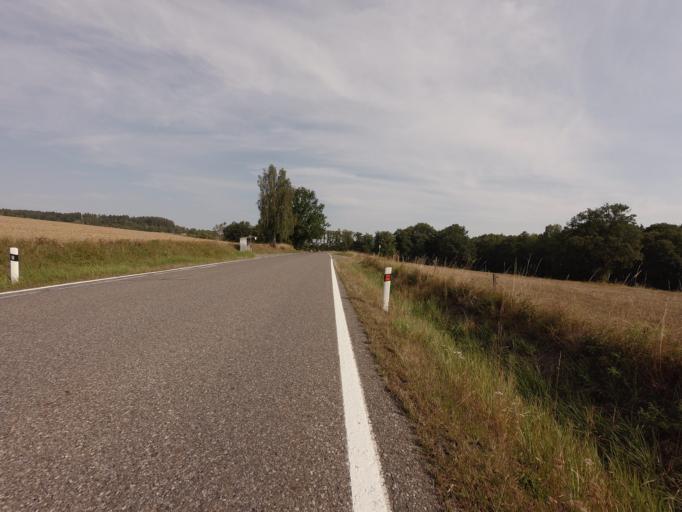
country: CZ
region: Jihocesky
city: Milevsko
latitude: 49.4914
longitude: 14.3641
